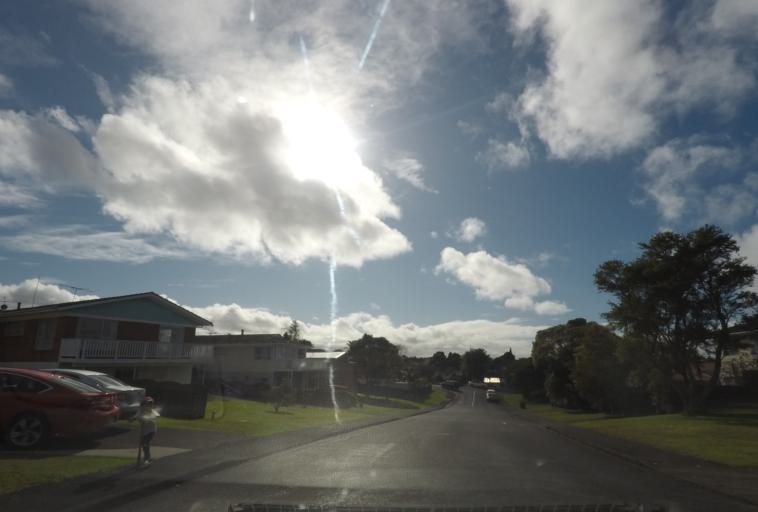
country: NZ
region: Auckland
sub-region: Auckland
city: Waitakere
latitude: -36.8961
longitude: 174.6519
